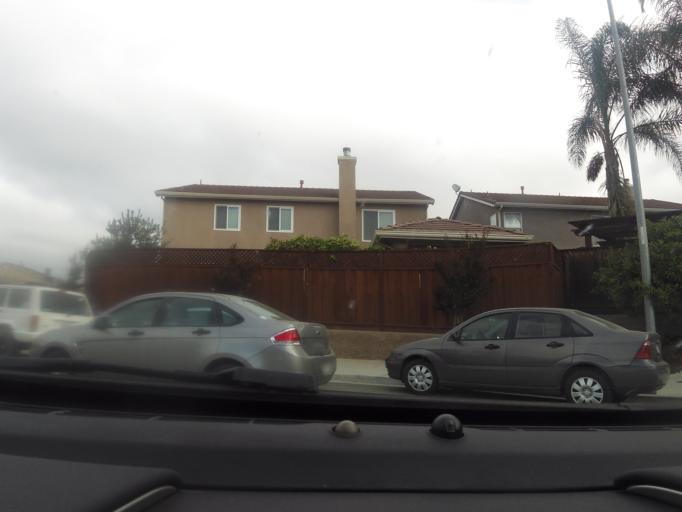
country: US
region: California
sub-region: San Benito County
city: Ridgemark
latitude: 36.8205
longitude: -121.3714
